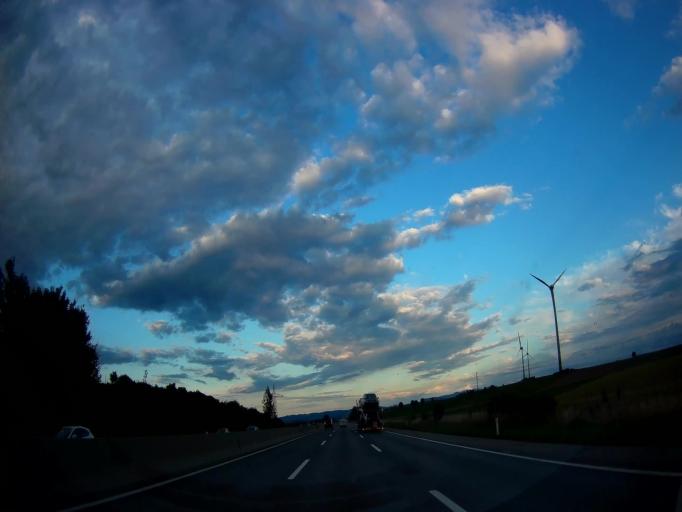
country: AT
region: Lower Austria
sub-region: Politischer Bezirk Sankt Polten
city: Haunoldstein
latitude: 48.1786
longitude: 15.4554
